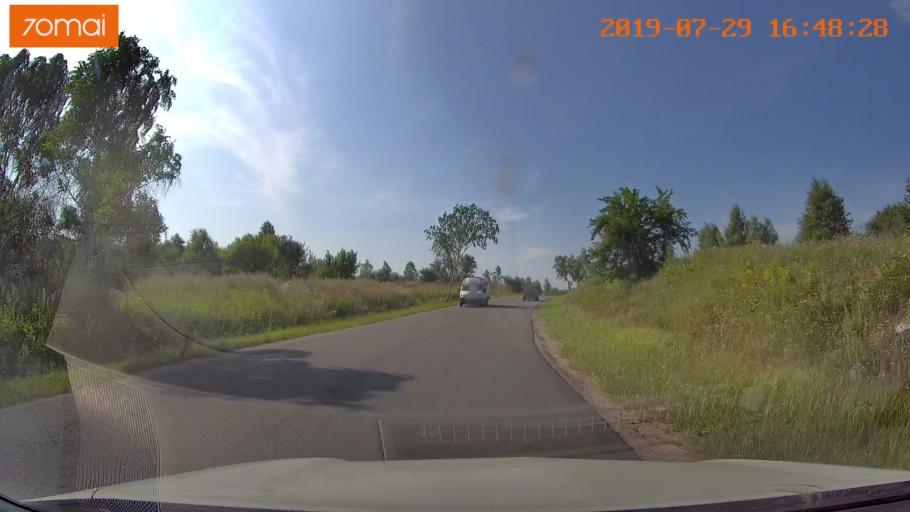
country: RU
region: Kaliningrad
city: Primorsk
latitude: 54.7869
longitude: 20.0768
